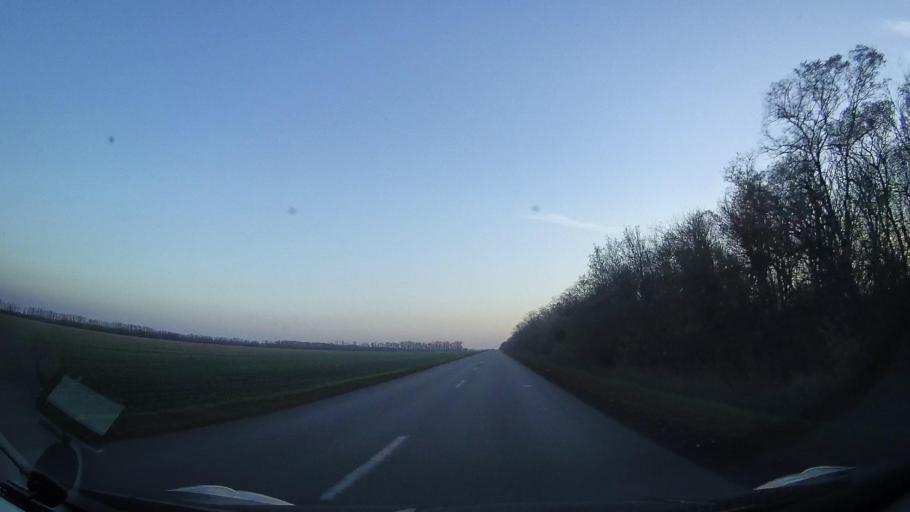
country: RU
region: Rostov
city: Zernograd
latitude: 47.0357
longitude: 40.3915
